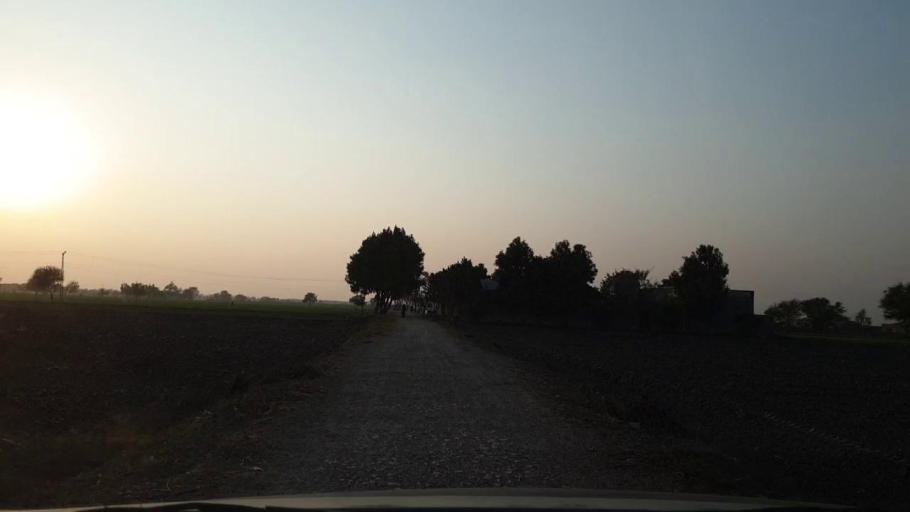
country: PK
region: Sindh
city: Tando Adam
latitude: 25.7143
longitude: 68.5791
